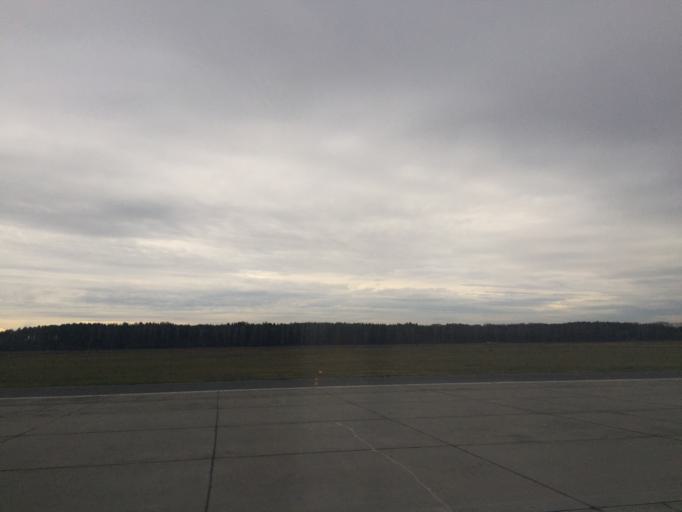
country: PL
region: Kujawsko-Pomorskie
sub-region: Bydgoszcz
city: Bydgoszcz
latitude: 53.0985
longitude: 17.9953
